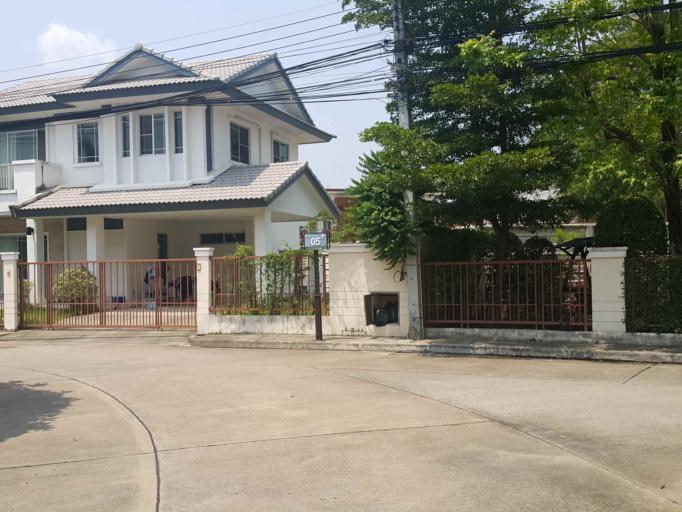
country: TH
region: Chiang Mai
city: Chiang Mai
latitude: 18.7488
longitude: 98.9534
